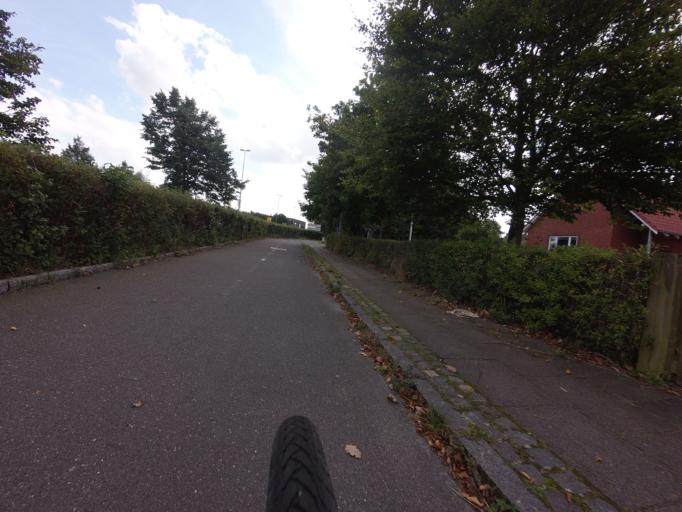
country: DK
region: Central Jutland
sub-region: Herning Kommune
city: Sunds
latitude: 56.1994
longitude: 9.0186
